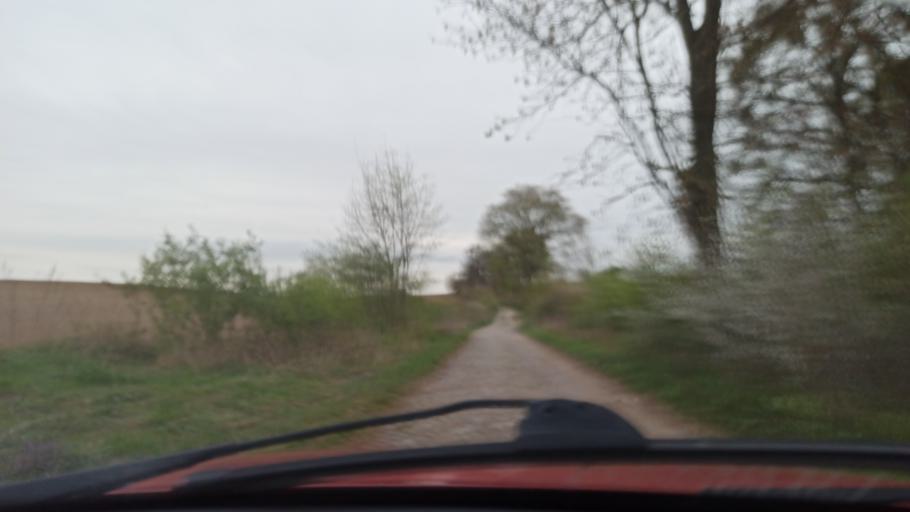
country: PL
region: Kujawsko-Pomorskie
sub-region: Powiat grudziadzki
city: Lasin
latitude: 53.5768
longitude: 19.0895
